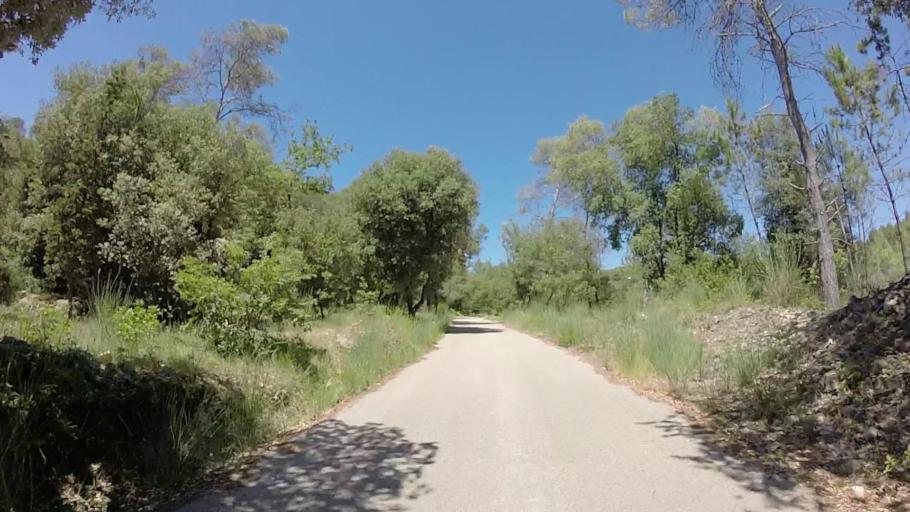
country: FR
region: Provence-Alpes-Cote d'Azur
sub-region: Departement des Alpes-Maritimes
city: Valbonne
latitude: 43.6302
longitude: 7.0267
